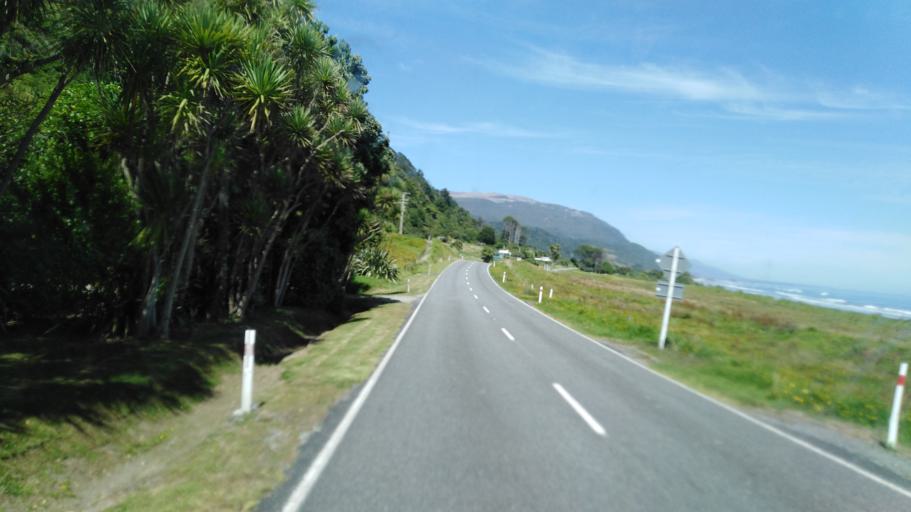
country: NZ
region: West Coast
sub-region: Buller District
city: Westport
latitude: -41.5915
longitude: 171.8901
